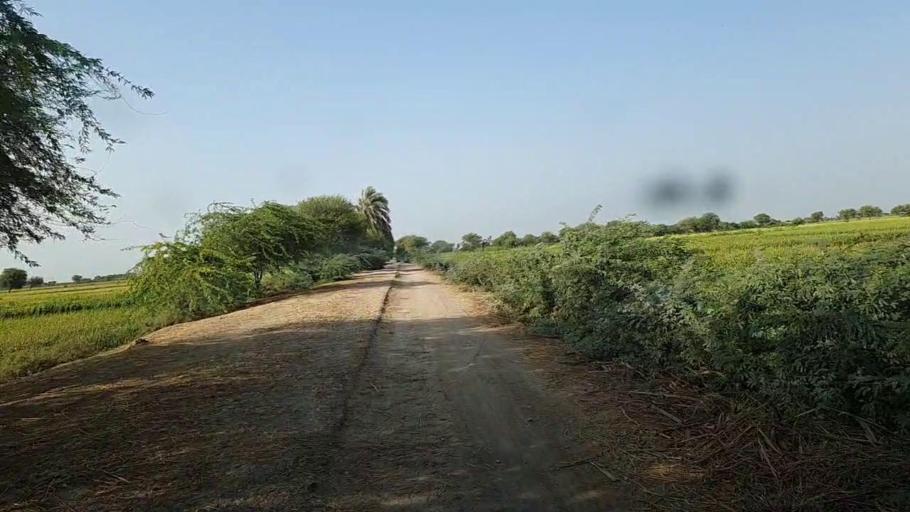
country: PK
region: Sindh
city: Bulri
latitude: 24.7780
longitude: 68.4336
